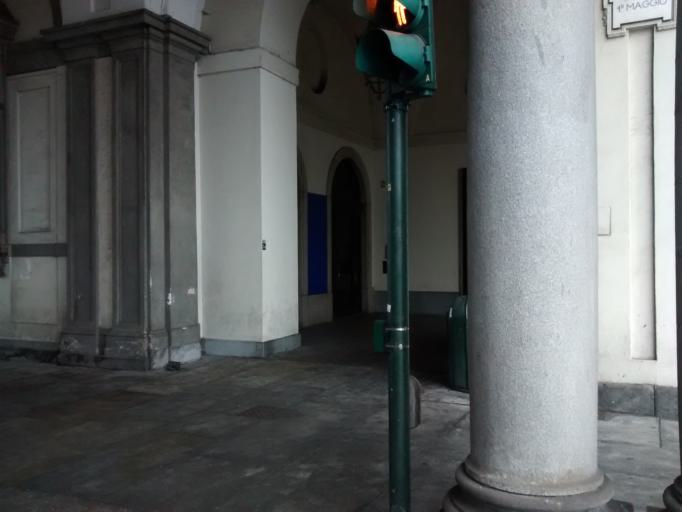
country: IT
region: Piedmont
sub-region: Provincia di Torino
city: Turin
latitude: 45.0711
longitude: 7.6874
